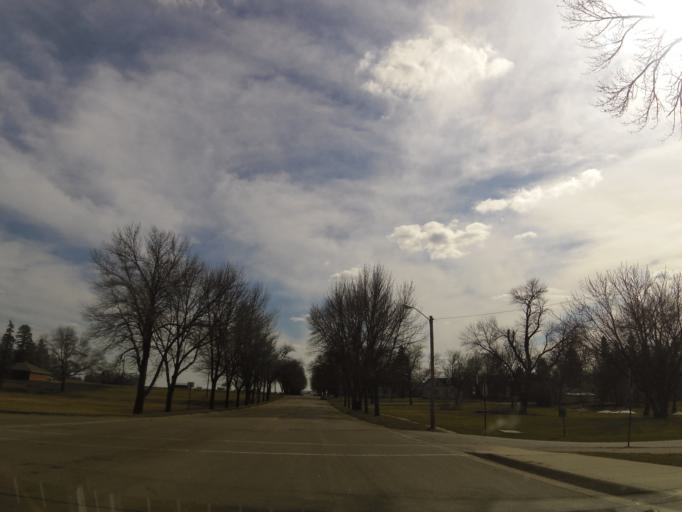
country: US
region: Minnesota
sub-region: Lac qui Parle County
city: Dawson
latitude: 44.9262
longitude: -96.0547
